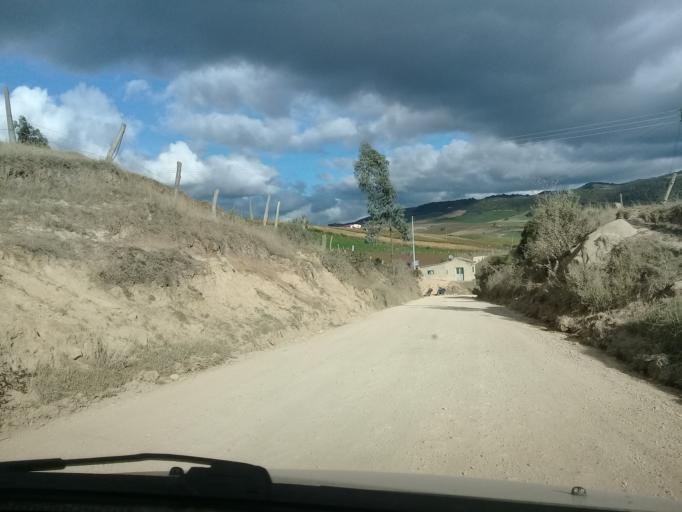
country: CO
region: Cundinamarca
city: Lenguazaque
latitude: 5.2791
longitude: -73.6575
